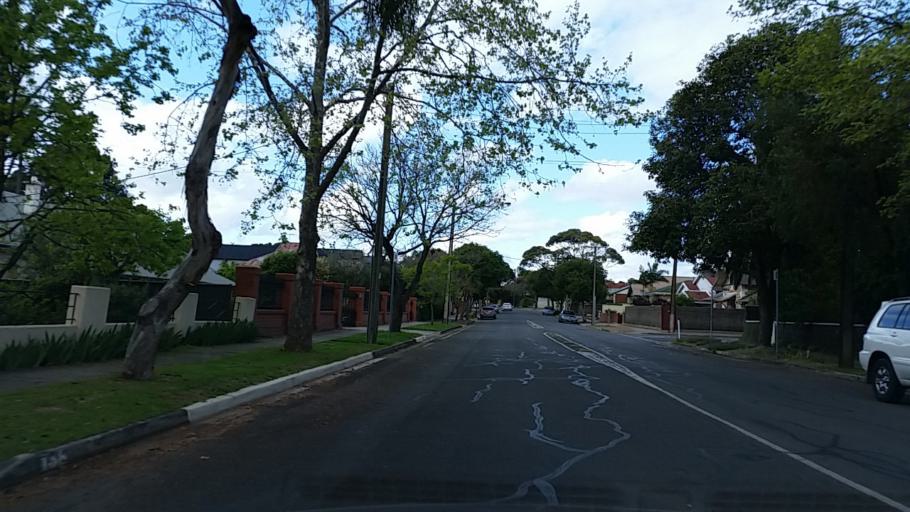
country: AU
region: South Australia
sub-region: Norwood Payneham St Peters
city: Royston Park
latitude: -34.8986
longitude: 138.6336
